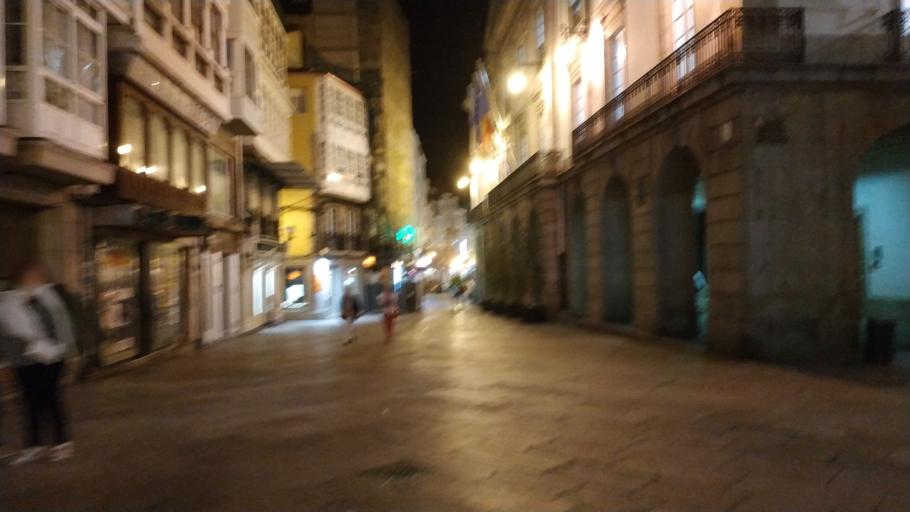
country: ES
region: Galicia
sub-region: Provincia da Coruna
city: A Coruna
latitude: 43.3704
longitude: -8.3990
